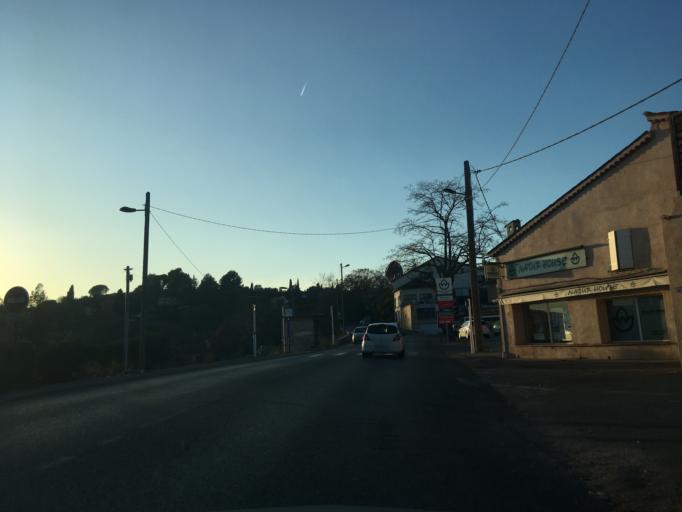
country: FR
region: Provence-Alpes-Cote d'Azur
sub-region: Departement des Alpes-Maritimes
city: Peymeinade
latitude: 43.6443
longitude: 6.9001
